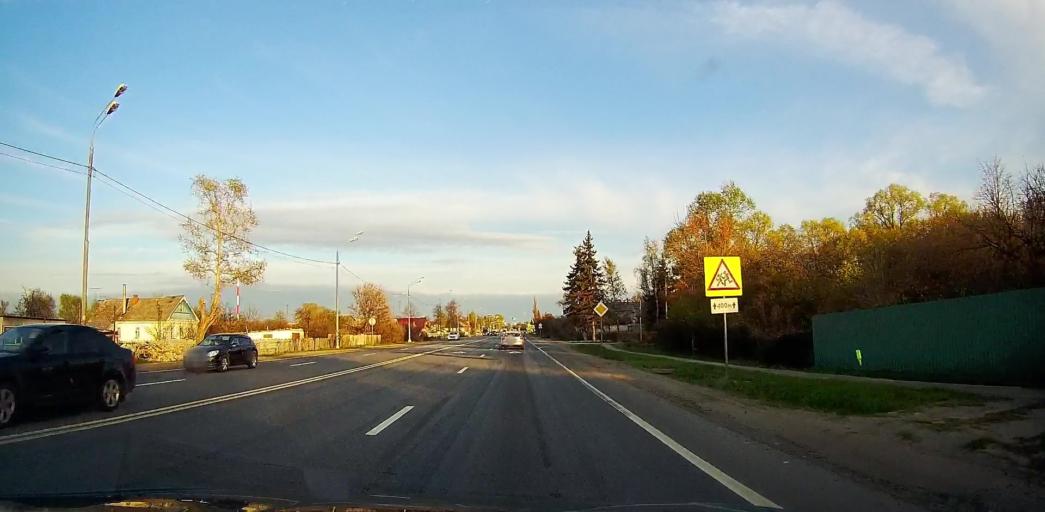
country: RU
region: Moskovskaya
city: Troitskoye
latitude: 55.2510
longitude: 38.5238
